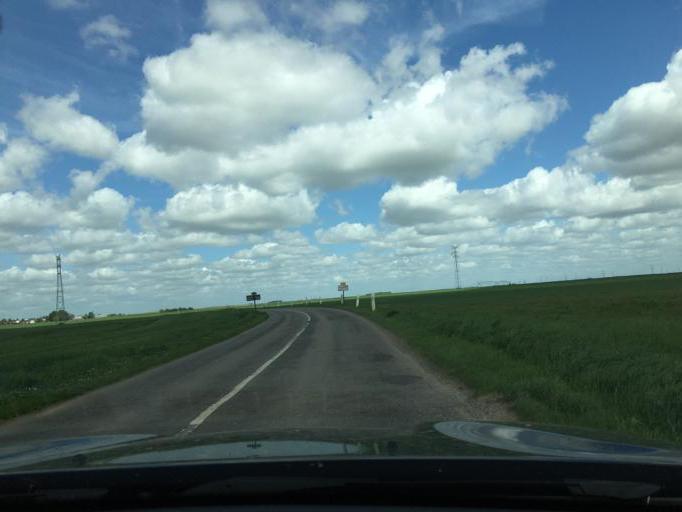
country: FR
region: Centre
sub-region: Departement du Loiret
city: Bricy
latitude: 48.0384
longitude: 1.8037
